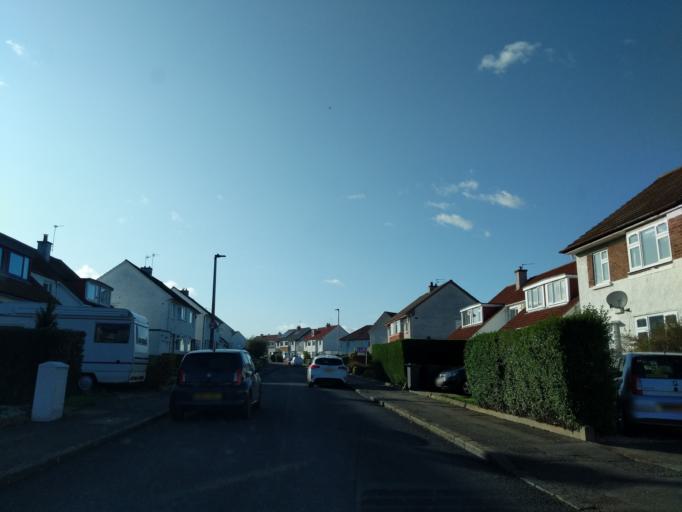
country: GB
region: Scotland
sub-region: Edinburgh
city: Colinton
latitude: 55.9675
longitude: -3.2631
